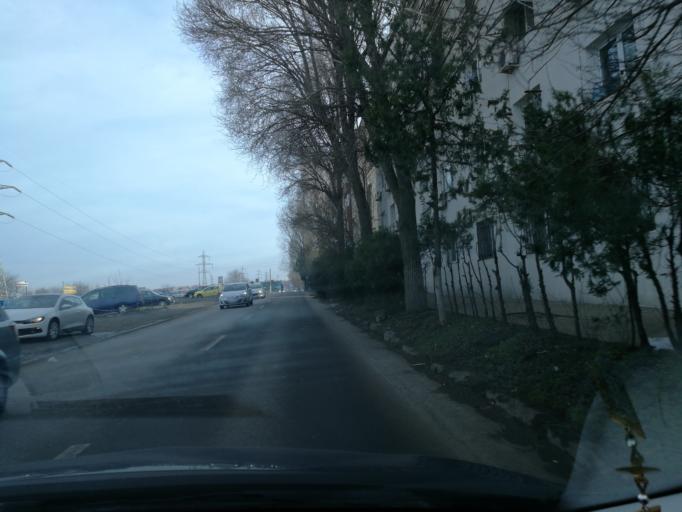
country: RO
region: Constanta
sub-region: Municipiul Constanta
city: Constanta
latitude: 44.1919
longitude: 28.6048
